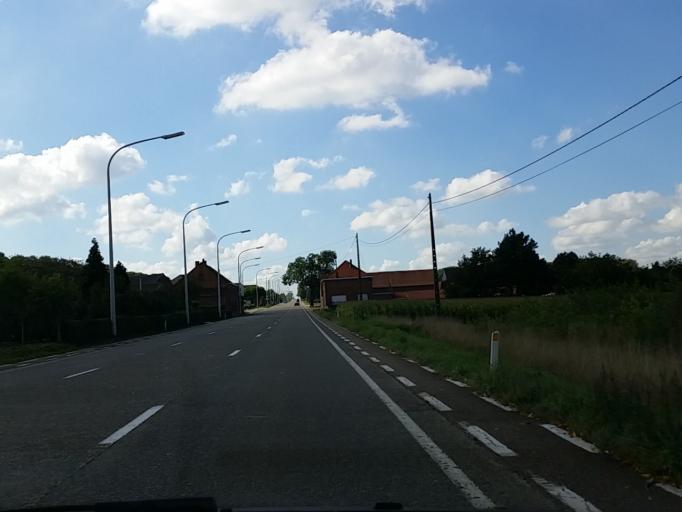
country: BE
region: Flanders
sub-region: Provincie Vlaams-Brabant
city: Bekkevoort
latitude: 50.9300
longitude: 4.9309
